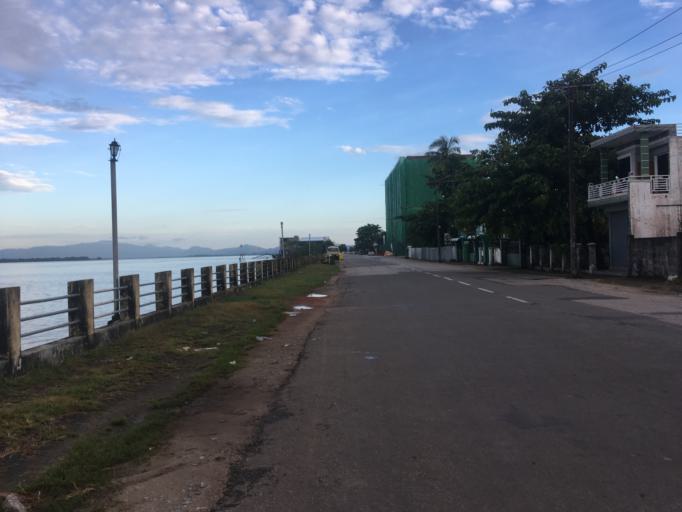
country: MM
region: Mon
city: Mawlamyine
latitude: 16.4691
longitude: 97.6215
